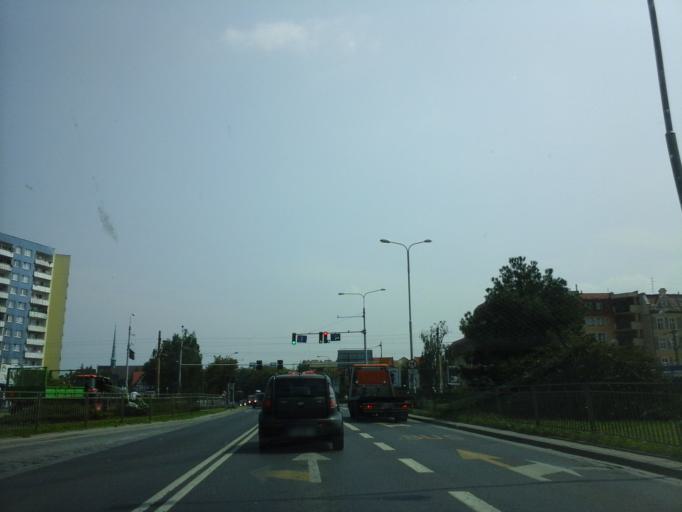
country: PL
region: Lower Silesian Voivodeship
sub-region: Powiat wroclawski
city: Wroclaw
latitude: 51.1358
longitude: 17.0354
